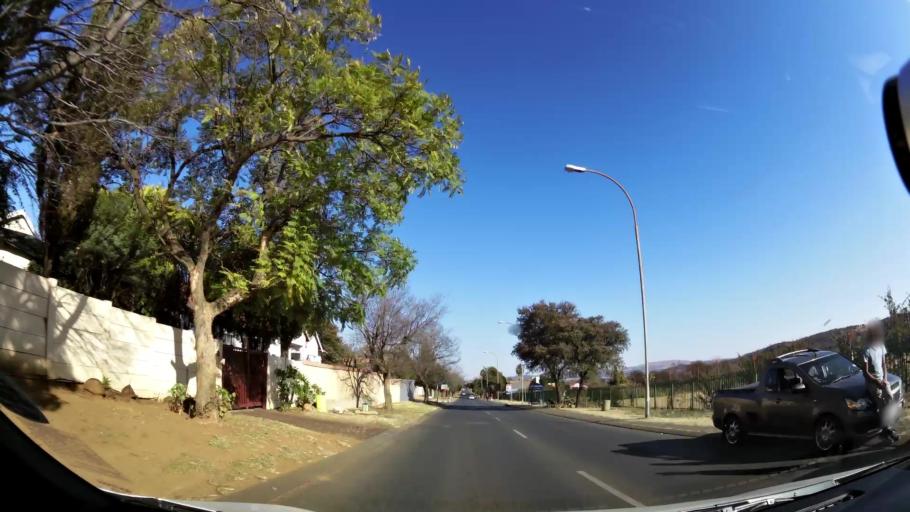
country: ZA
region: Gauteng
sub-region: City of Johannesburg Metropolitan Municipality
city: Johannesburg
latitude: -26.2919
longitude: 28.0540
